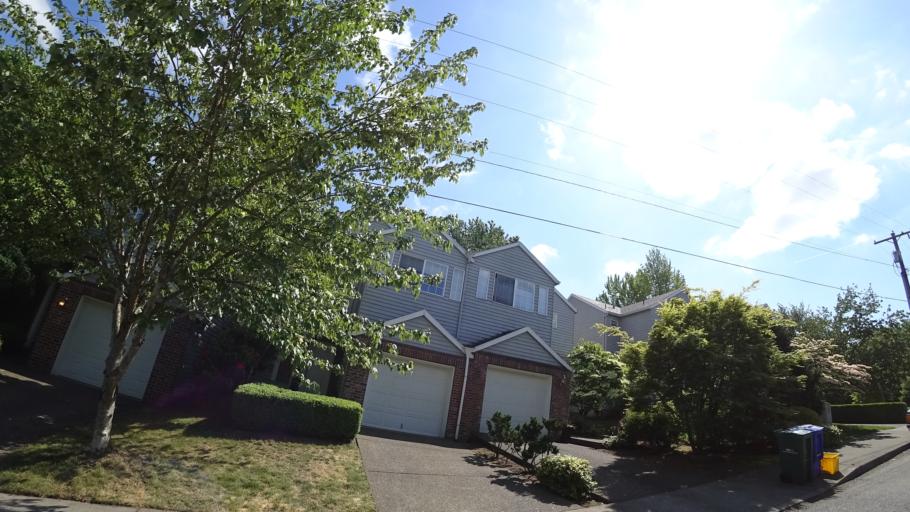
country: US
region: Oregon
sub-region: Washington County
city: Garden Home-Whitford
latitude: 45.4737
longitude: -122.7080
